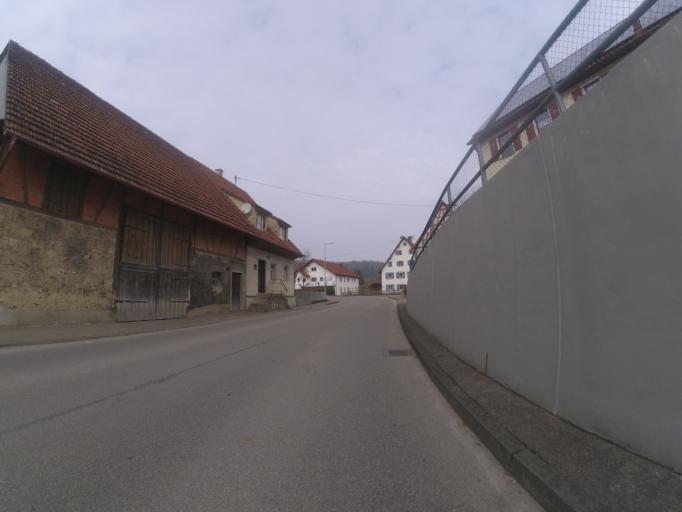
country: DE
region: Baden-Wuerttemberg
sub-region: Tuebingen Region
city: Hayingen
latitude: 48.2928
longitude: 9.4947
